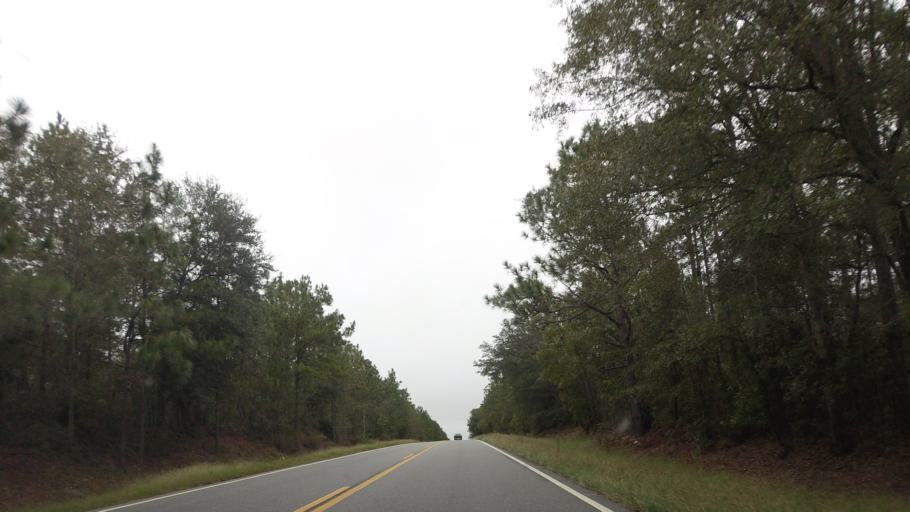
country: US
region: Georgia
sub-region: Berrien County
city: Enigma
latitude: 31.4069
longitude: -83.2415
